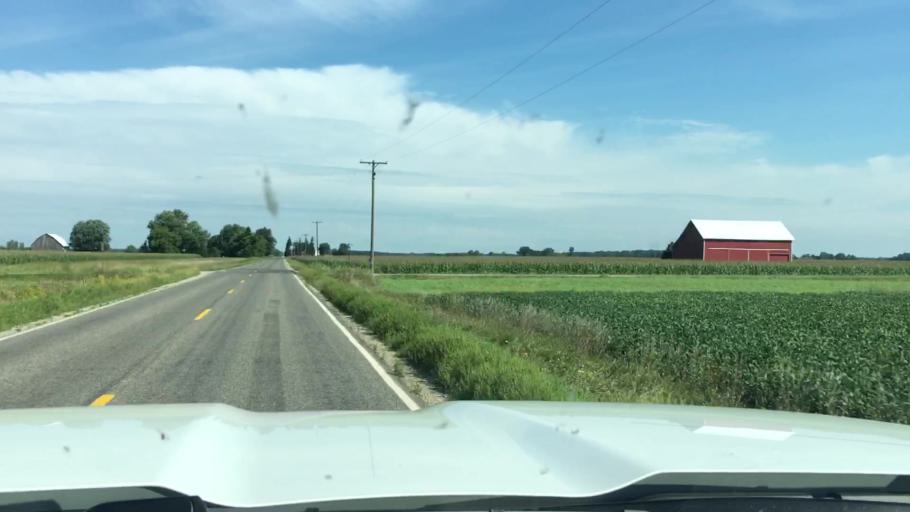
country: US
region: Michigan
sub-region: Saginaw County
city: Hemlock
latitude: 43.5099
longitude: -84.2296
